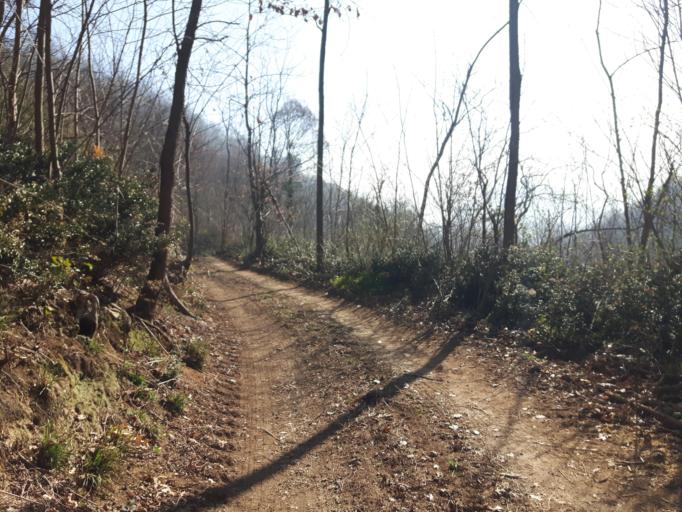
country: IT
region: Veneto
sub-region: Provincia di Padova
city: Vo
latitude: 45.3523
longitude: 11.6633
